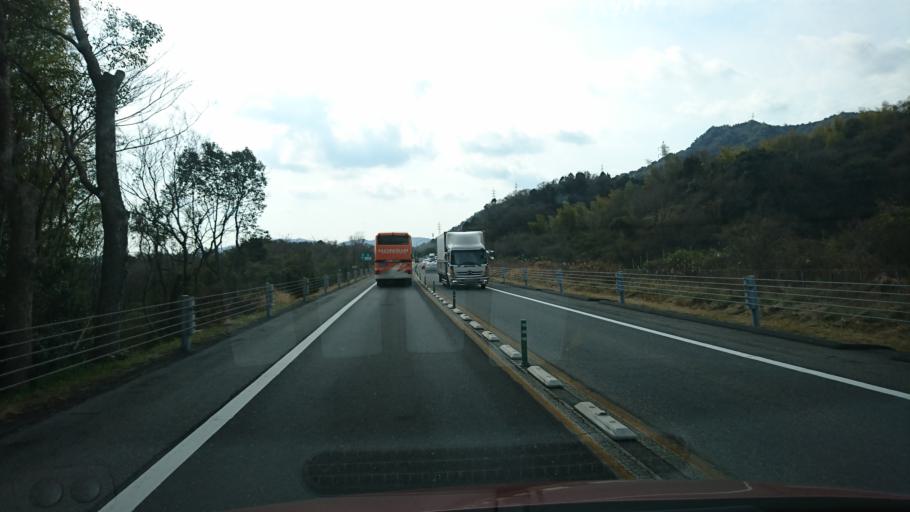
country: JP
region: Hiroshima
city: Innoshima
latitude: 34.2338
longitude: 133.0480
